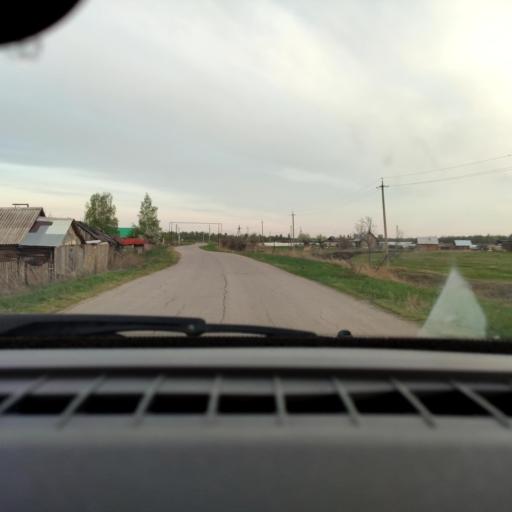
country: RU
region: Samara
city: Georgiyevka
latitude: 53.2711
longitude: 50.9579
